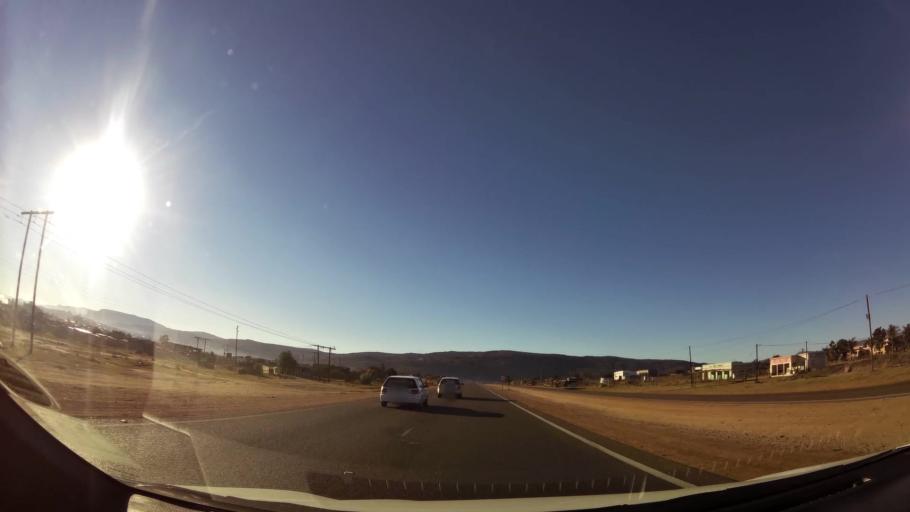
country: ZA
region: Limpopo
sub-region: Capricorn District Municipality
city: Mankoeng
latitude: -23.9115
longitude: 29.7790
